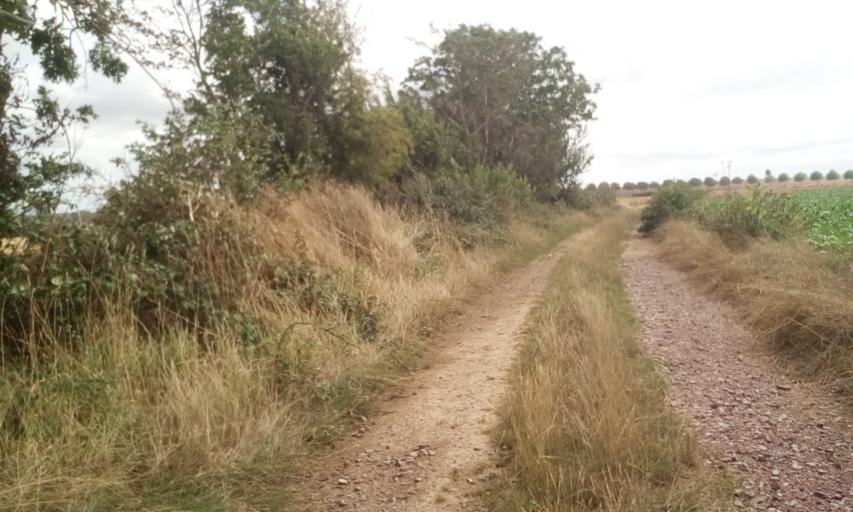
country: FR
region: Lower Normandy
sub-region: Departement du Calvados
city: Cheux
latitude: 49.1817
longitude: -0.5433
